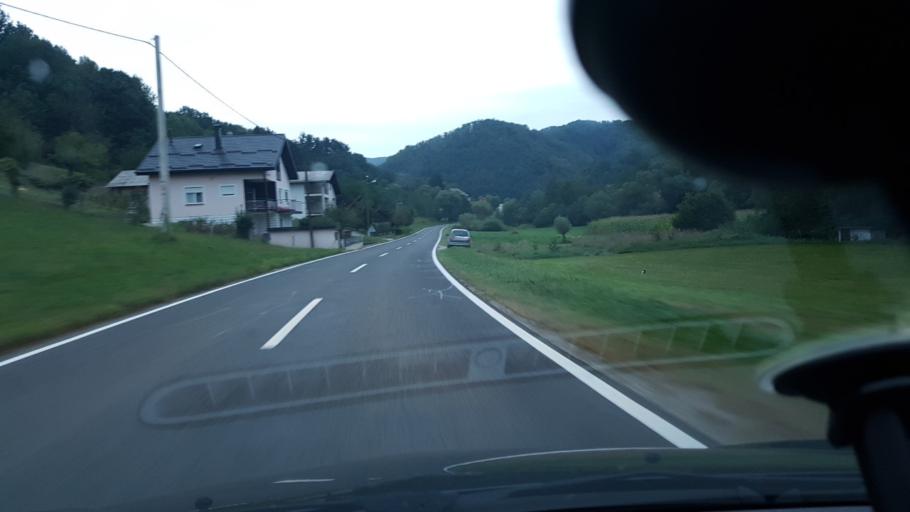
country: HR
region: Krapinsko-Zagorska
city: Pregrada
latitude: 46.2119
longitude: 15.7497
